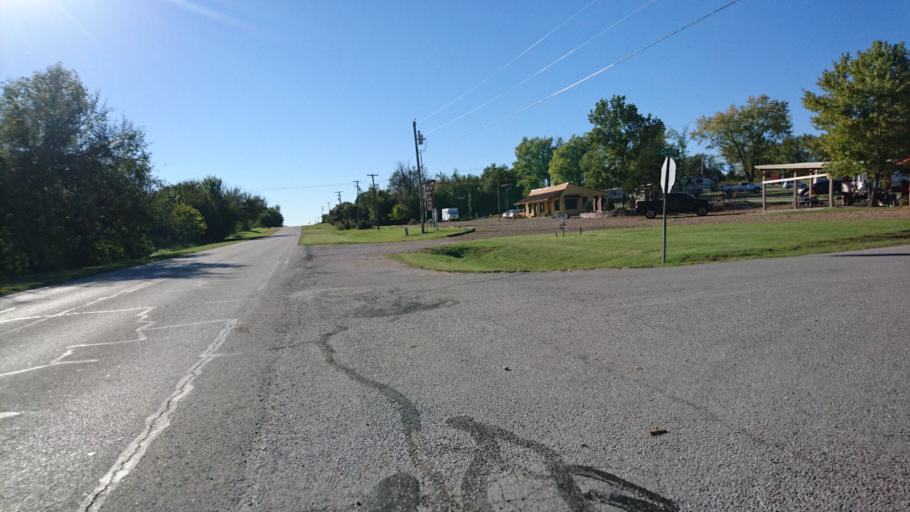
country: US
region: Missouri
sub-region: Jasper County
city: Carthage
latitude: 37.1732
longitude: -94.3758
